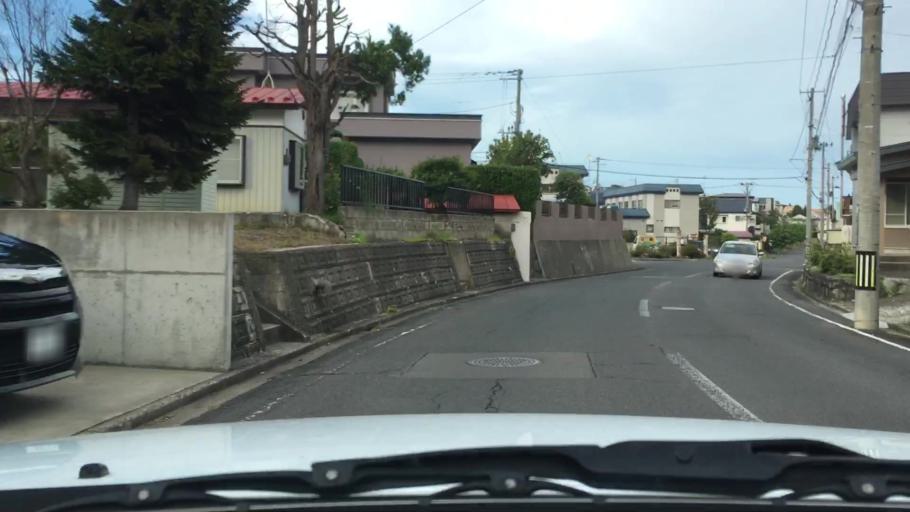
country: JP
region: Aomori
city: Hirosaki
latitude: 40.5756
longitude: 140.4540
